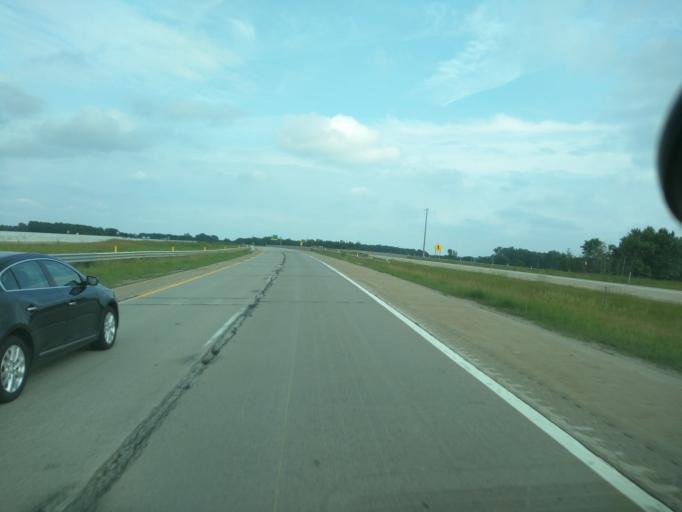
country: US
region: Michigan
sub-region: Clinton County
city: DeWitt
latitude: 42.8079
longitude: -84.5138
